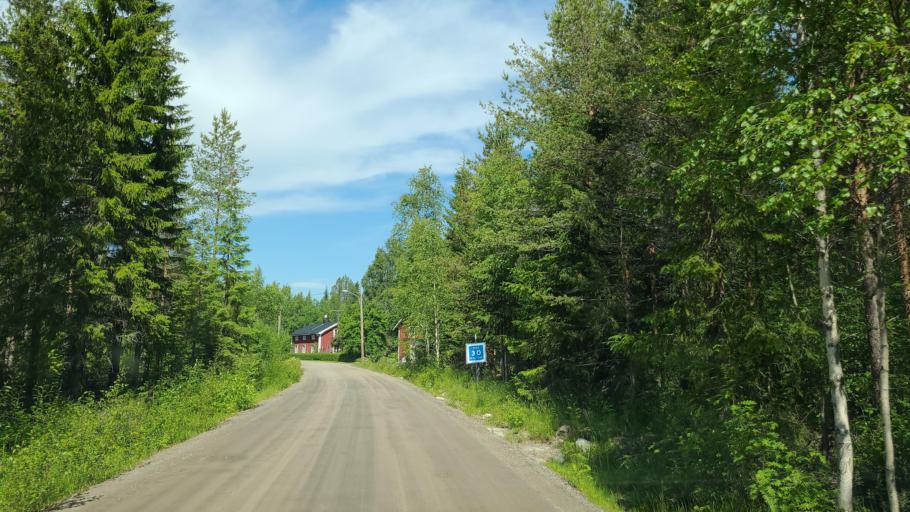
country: SE
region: Vaesterbotten
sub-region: Robertsfors Kommun
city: Robertsfors
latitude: 64.1525
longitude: 20.9505
